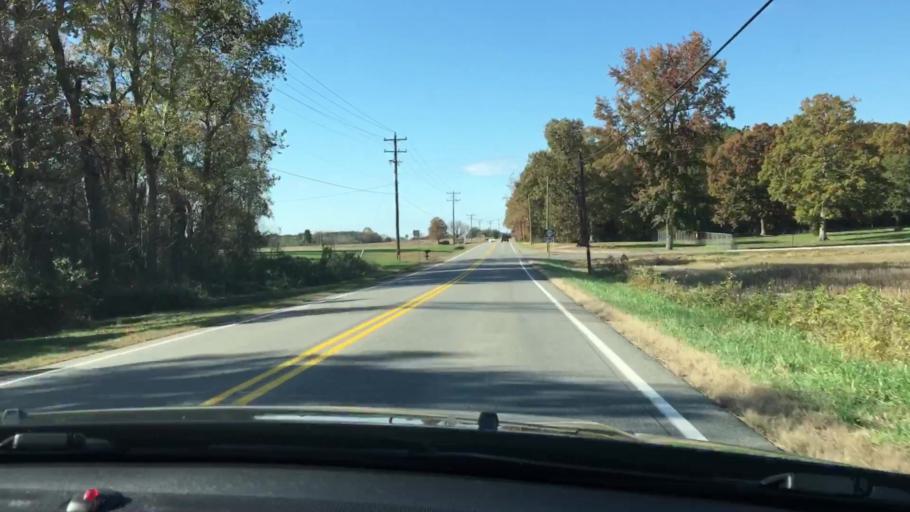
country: US
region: Virginia
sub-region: King William County
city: Central Garage
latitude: 37.7212
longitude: -77.0820
